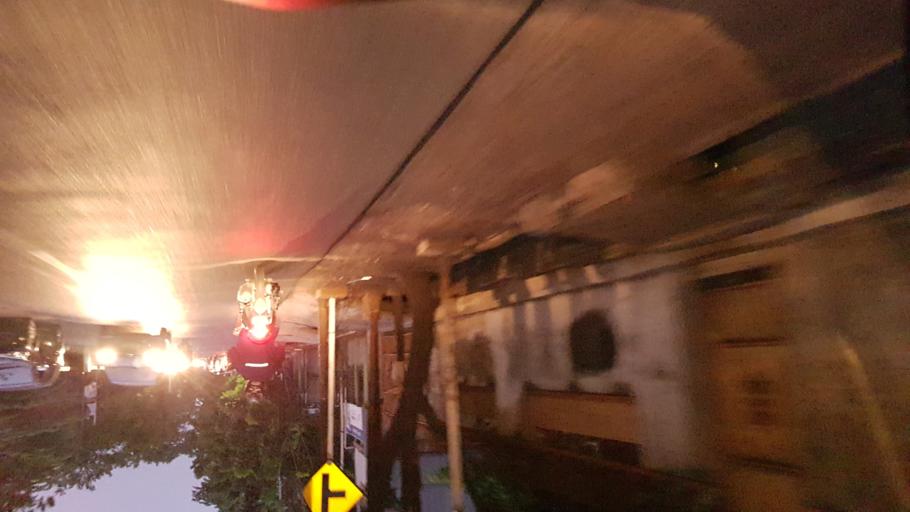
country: ID
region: Jakarta Raya
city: Jakarta
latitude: -6.2995
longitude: 106.8262
